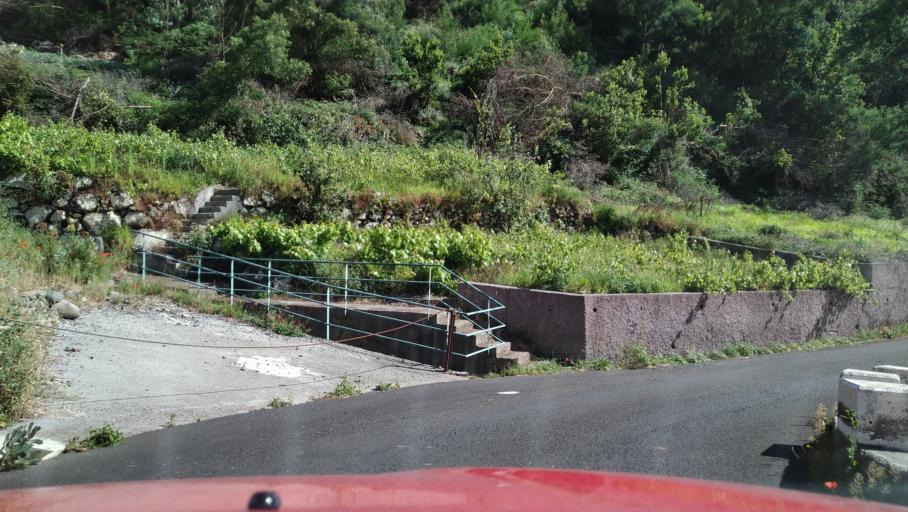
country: PT
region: Madeira
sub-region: Machico
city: Canical
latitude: 32.7394
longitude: -16.7714
